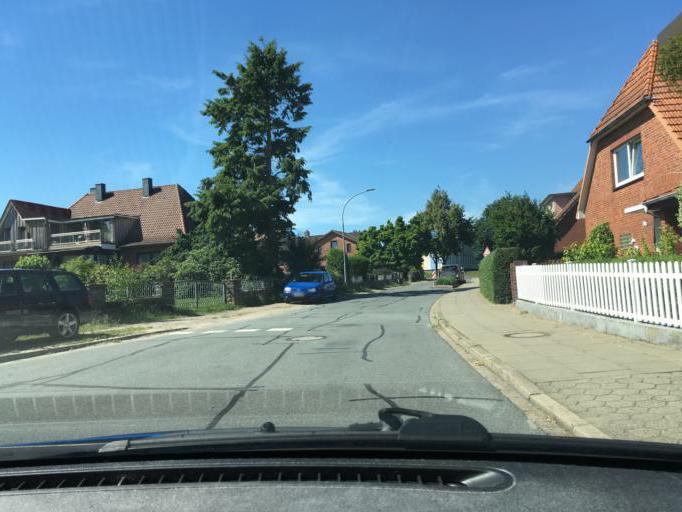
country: DE
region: Lower Saxony
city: Buchholz in der Nordheide
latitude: 53.3808
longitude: 9.8892
